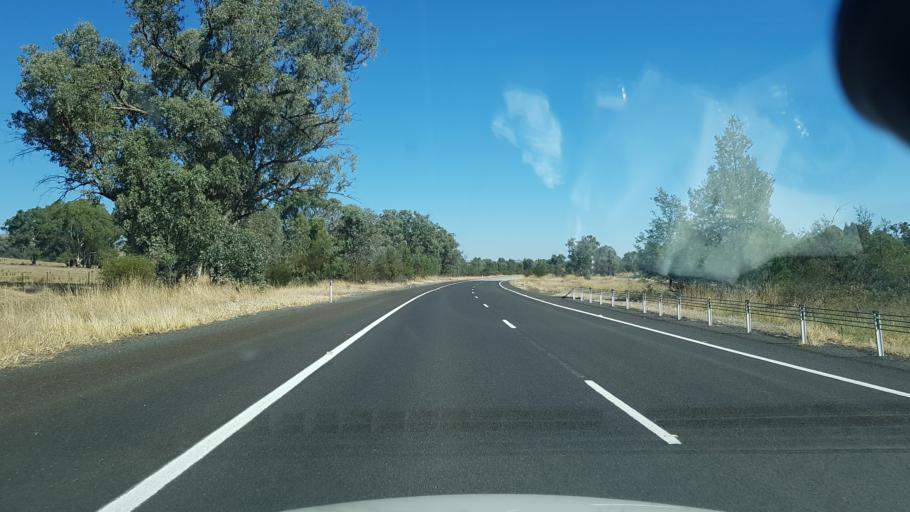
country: AU
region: New South Wales
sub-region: Greater Hume Shire
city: Holbrook
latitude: -35.8900
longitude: 147.1729
